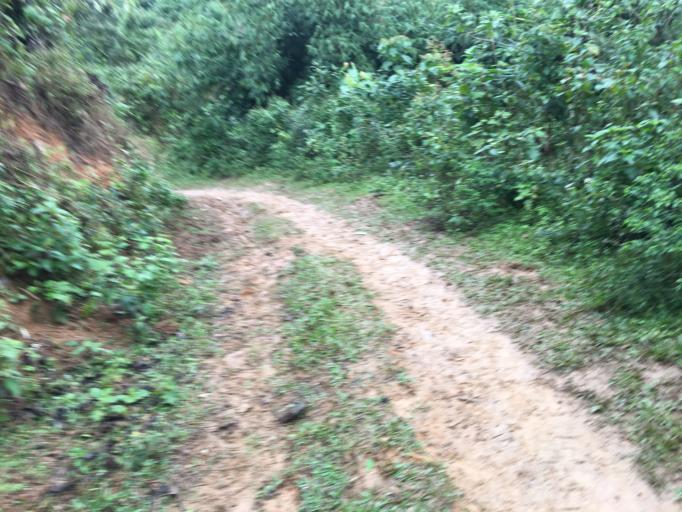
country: LA
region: Houaphan
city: Xamtay
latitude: 19.8991
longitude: 104.4597
